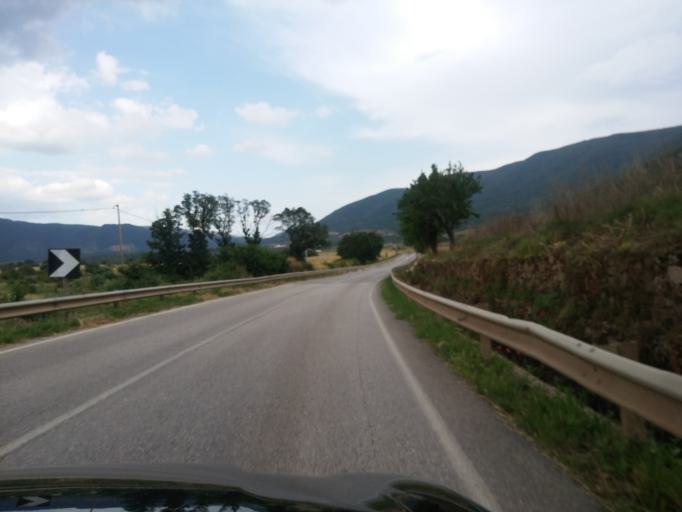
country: IT
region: Apulia
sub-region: Provincia di Foggia
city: Rignano Garganico
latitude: 41.7151
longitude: 15.5283
